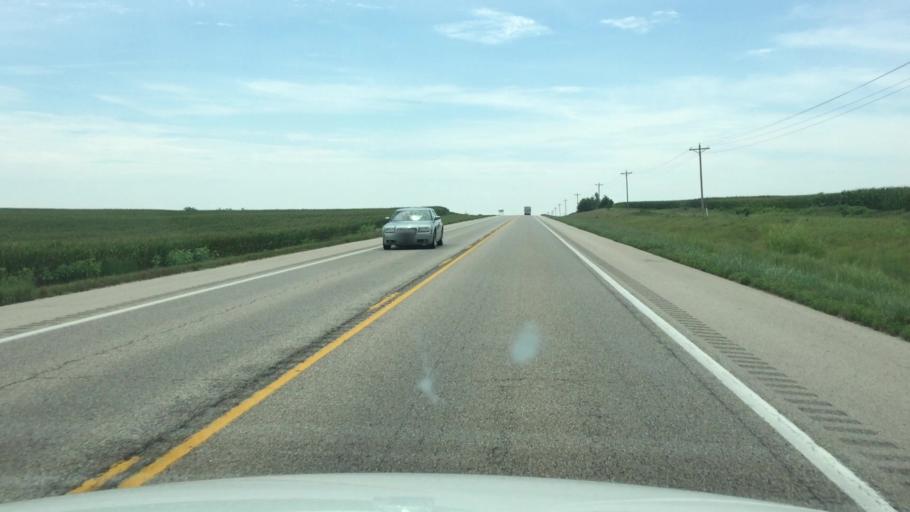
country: US
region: Kansas
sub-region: Nemaha County
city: Sabetha
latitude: 39.7180
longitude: -95.7299
